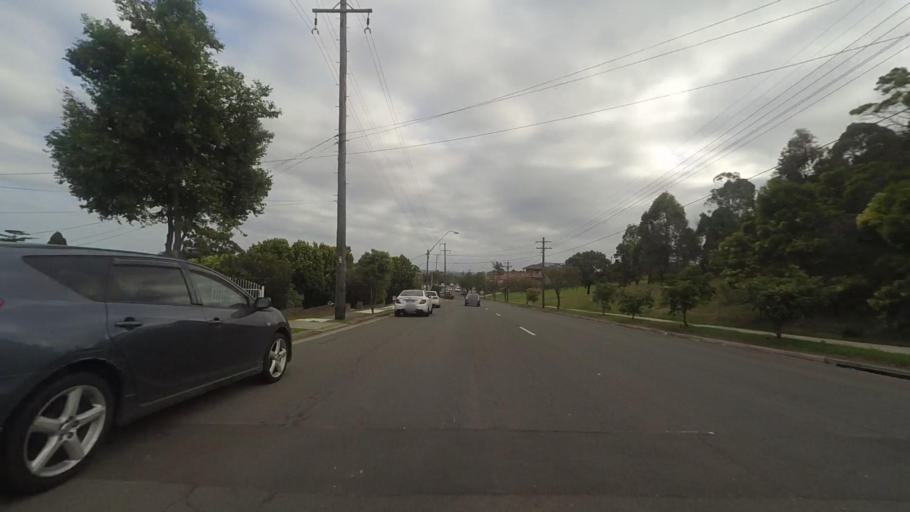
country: AU
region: New South Wales
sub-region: Bankstown
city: Bankstown
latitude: -33.9182
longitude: 151.0137
